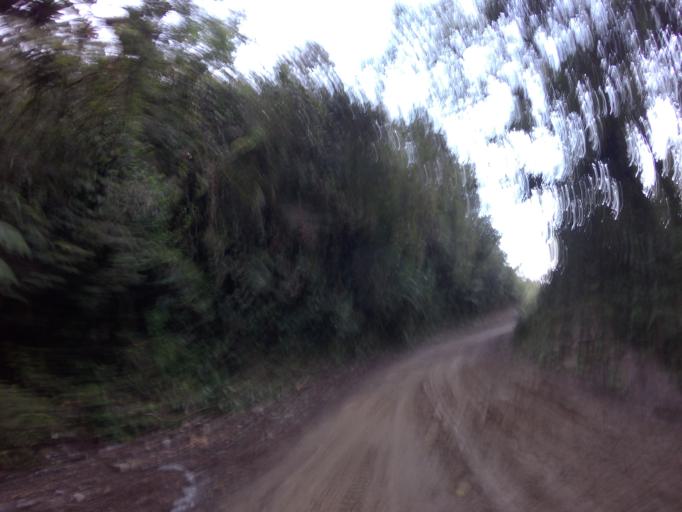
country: CO
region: Caldas
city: Pensilvania
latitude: 5.4502
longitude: -75.1271
